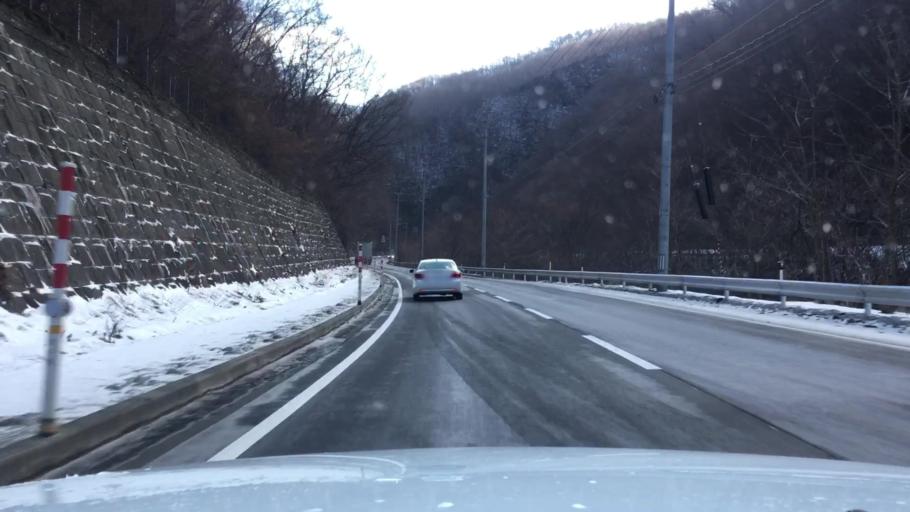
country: JP
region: Iwate
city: Tono
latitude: 39.6446
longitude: 141.5487
